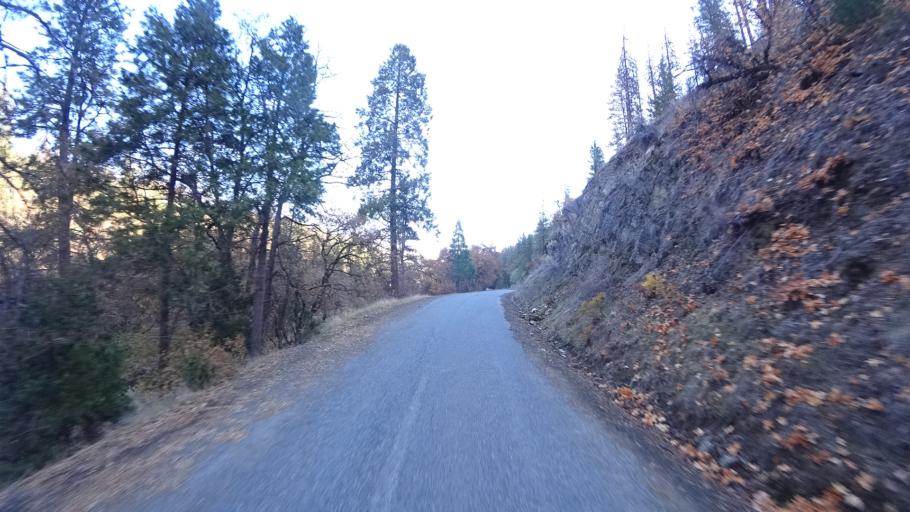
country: US
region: California
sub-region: Siskiyou County
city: Yreka
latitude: 41.8334
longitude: -122.9468
